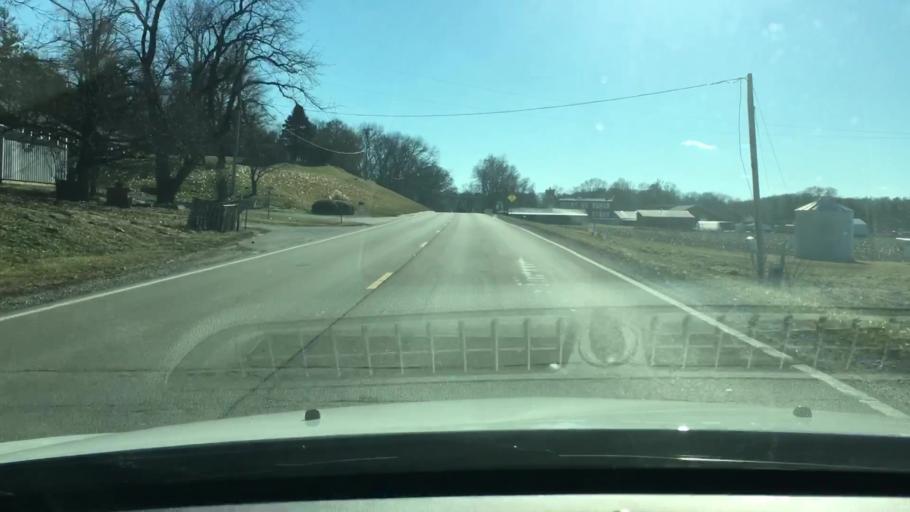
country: US
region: Illinois
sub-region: Morgan County
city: Meredosia
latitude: 39.7577
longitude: -90.5351
